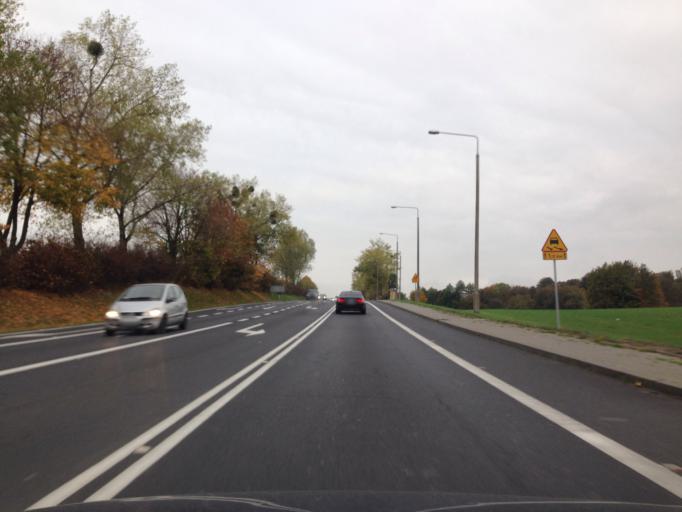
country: PL
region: Kujawsko-Pomorskie
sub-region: Powiat swiecki
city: Pruszcz
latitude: 53.3098
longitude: 18.2617
